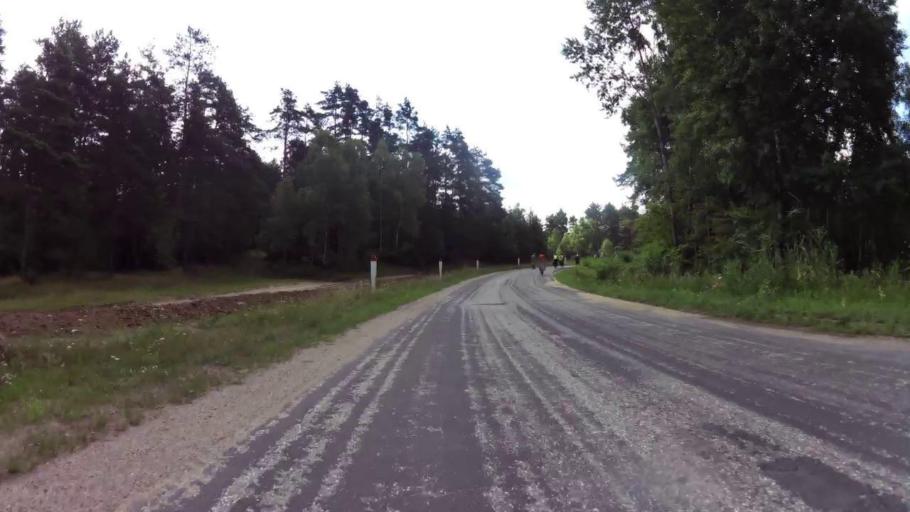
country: PL
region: West Pomeranian Voivodeship
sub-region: Powiat drawski
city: Drawsko Pomorskie
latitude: 53.4600
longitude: 15.7790
